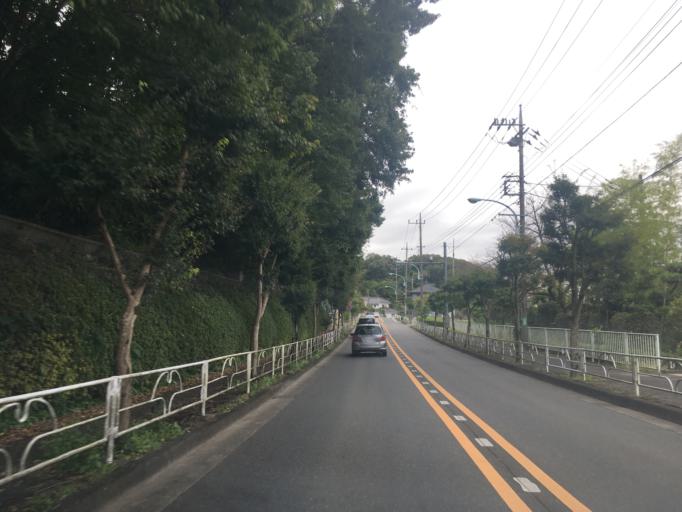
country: JP
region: Tokyo
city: Fussa
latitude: 35.7625
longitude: 139.3878
